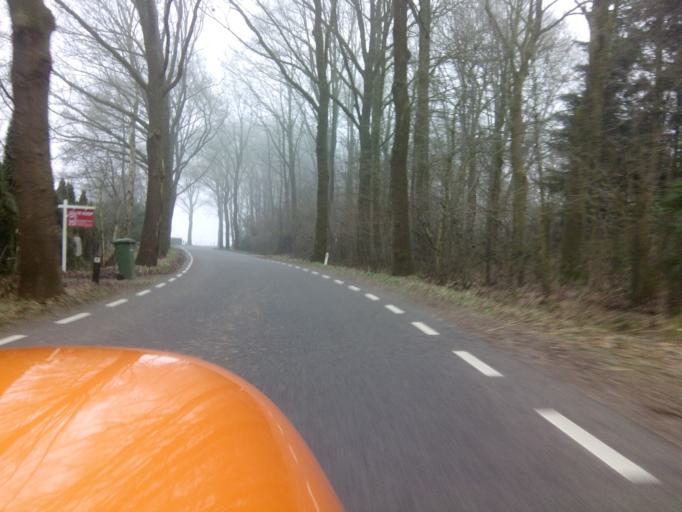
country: NL
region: Utrecht
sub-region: Gemeente Leusden
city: Leusden
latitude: 52.1586
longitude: 5.4593
